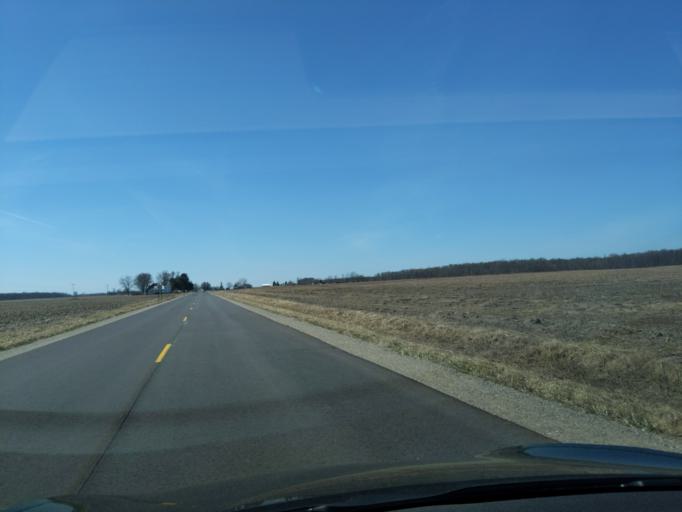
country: US
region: Michigan
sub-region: Eaton County
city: Grand Ledge
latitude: 42.7267
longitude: -84.8773
